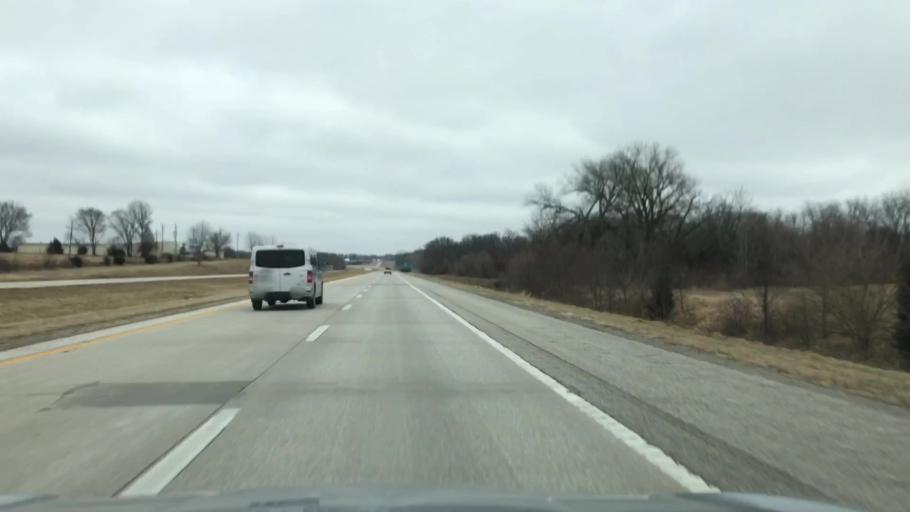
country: US
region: Missouri
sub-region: Linn County
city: Brookfield
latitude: 39.7773
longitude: -93.0955
